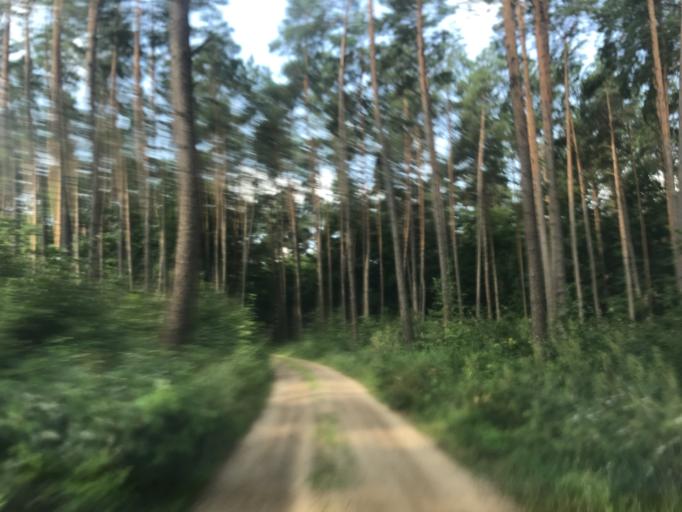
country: PL
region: Warmian-Masurian Voivodeship
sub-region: Powiat nowomiejski
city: Kurzetnik
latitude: 53.3501
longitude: 19.4733
